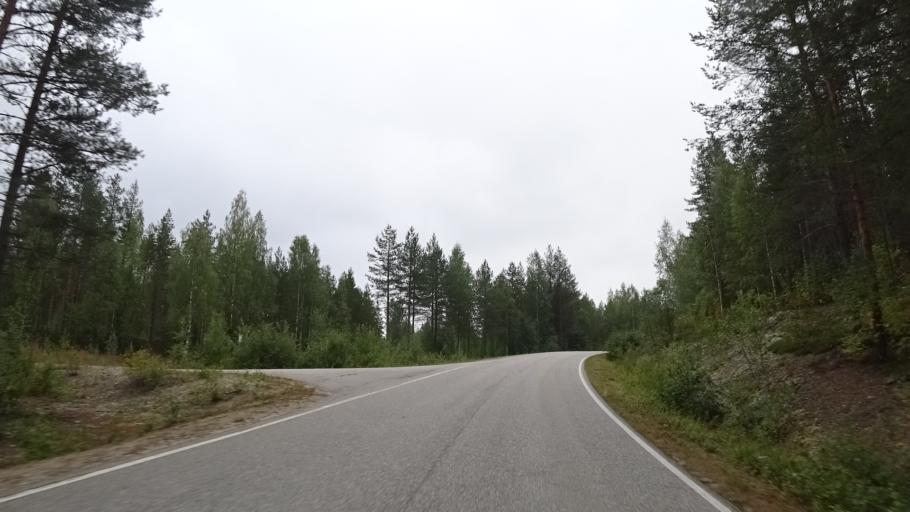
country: FI
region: North Karelia
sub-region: Pielisen Karjala
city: Lieksa
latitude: 63.3268
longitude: 30.2399
